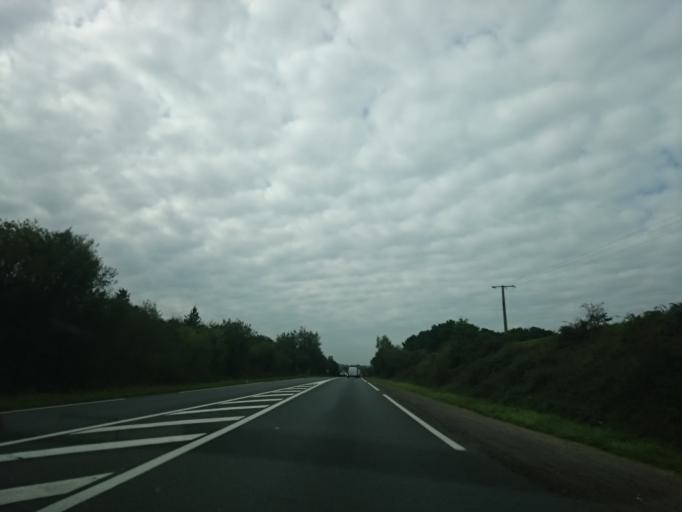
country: FR
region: Pays de la Loire
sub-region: Departement de la Loire-Atlantique
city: Saint-Herblain
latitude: 47.2185
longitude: -1.6574
